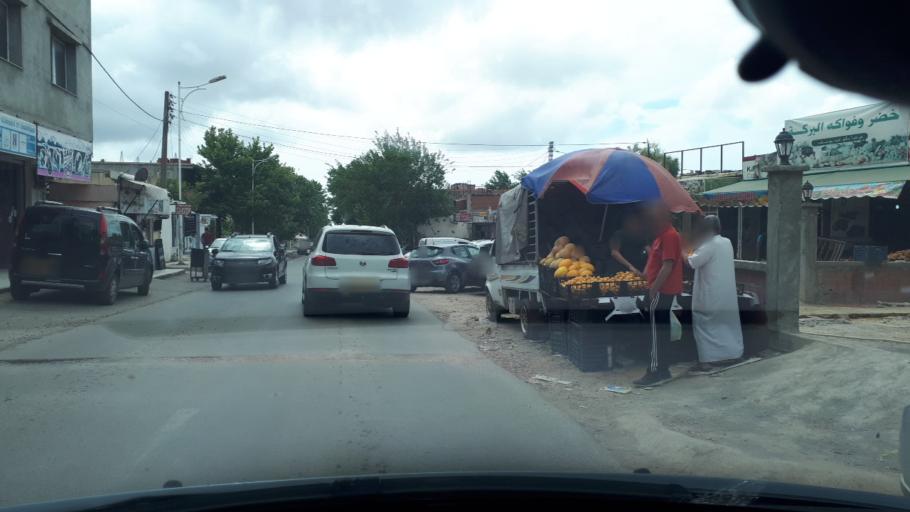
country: DZ
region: Tipaza
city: Cheraga
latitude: 36.7430
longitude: 2.9096
